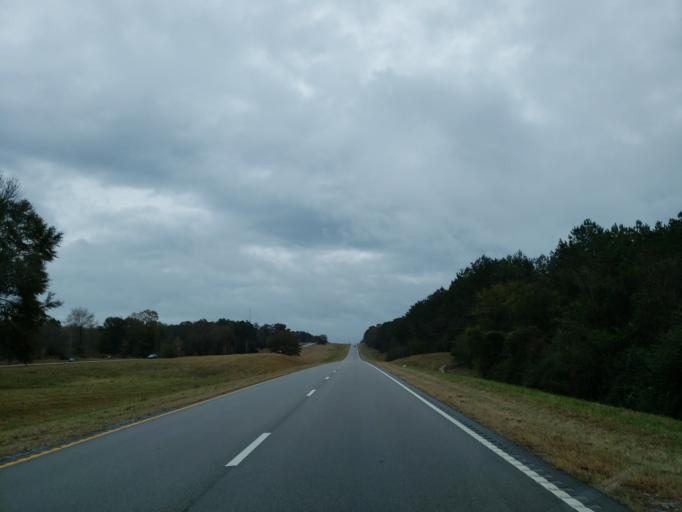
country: US
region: Mississippi
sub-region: Wayne County
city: Waynesboro
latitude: 31.6951
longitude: -88.7577
